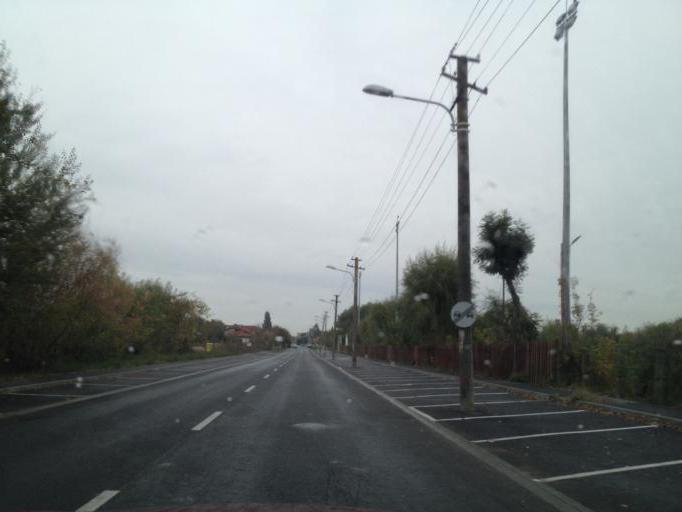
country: RO
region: Dolj
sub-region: Municipiul Craiova
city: Mofleni
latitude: 44.3112
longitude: 23.7679
